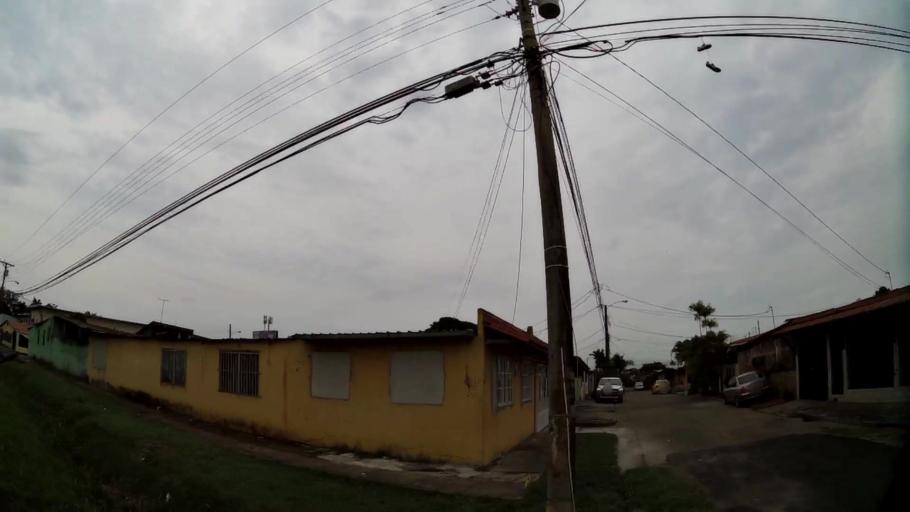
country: PA
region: Panama
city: San Miguelito
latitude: 9.0476
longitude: -79.4451
